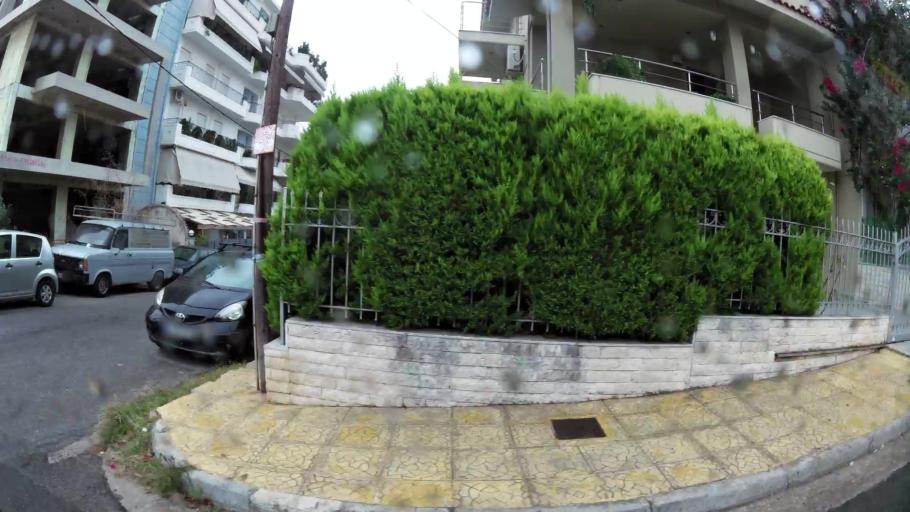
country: GR
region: Attica
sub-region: Nomos Piraios
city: Korydallos
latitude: 37.9864
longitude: 23.6299
